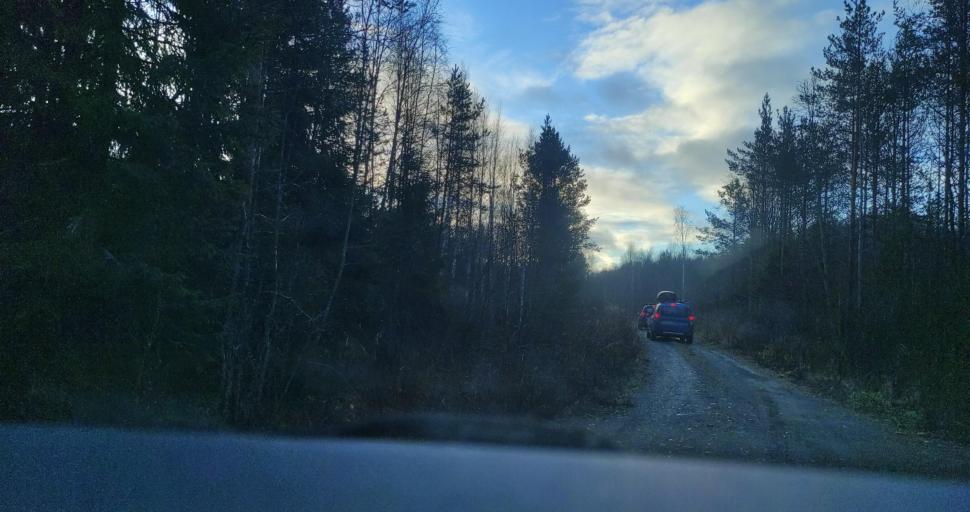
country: RU
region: Republic of Karelia
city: Pitkyaranta
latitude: 61.7327
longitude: 31.3787
